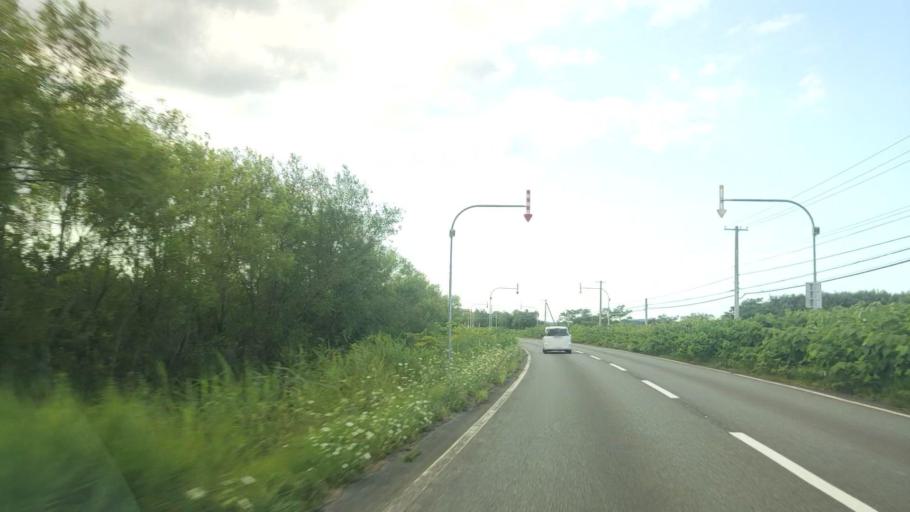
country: JP
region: Hokkaido
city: Makubetsu
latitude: 44.9993
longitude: 141.8167
